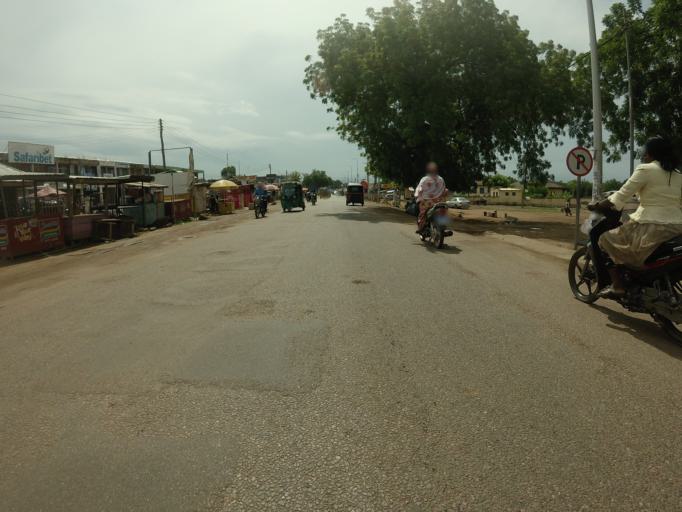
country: GH
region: Upper East
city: Bolgatanga
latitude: 10.7830
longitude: -0.8502
